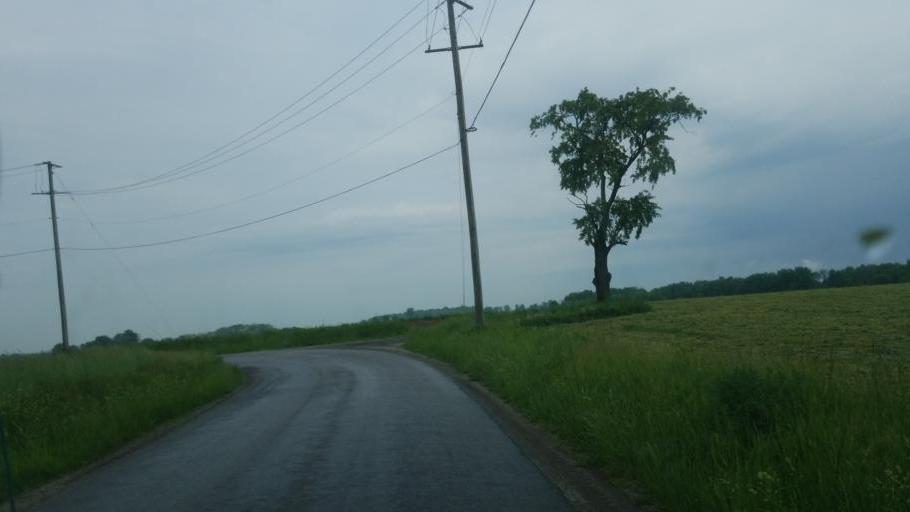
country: US
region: Ohio
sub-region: Wayne County
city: Dalton
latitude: 40.8141
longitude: -81.7258
